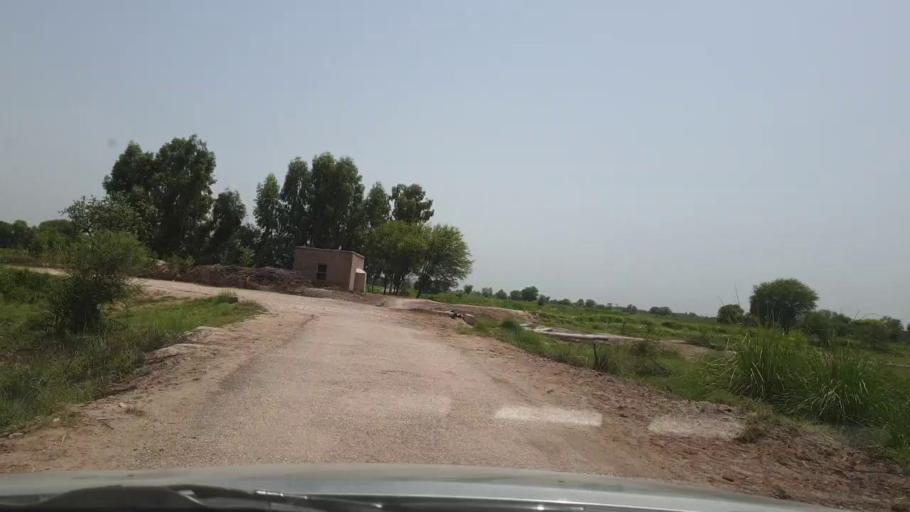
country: PK
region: Sindh
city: Pano Aqil
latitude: 27.8217
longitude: 69.2225
